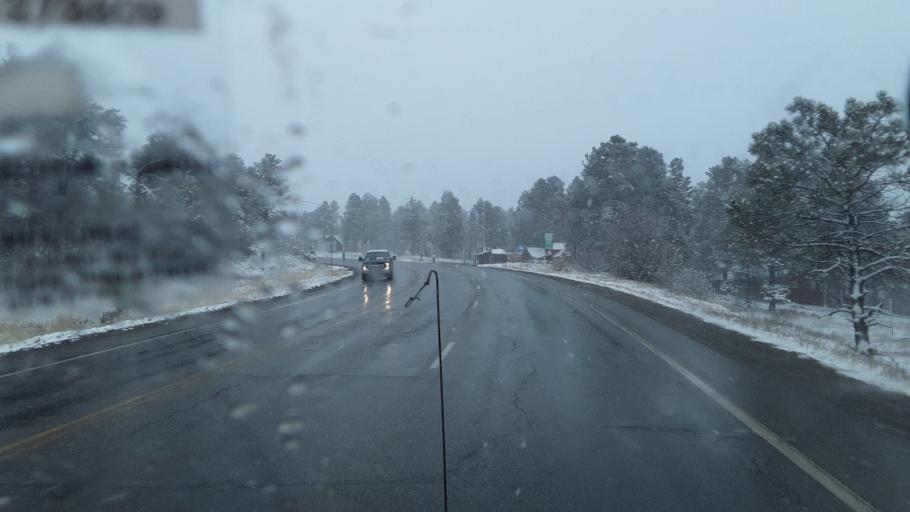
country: US
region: Colorado
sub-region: Archuleta County
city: Pagosa Springs
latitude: 37.2723
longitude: -107.0330
